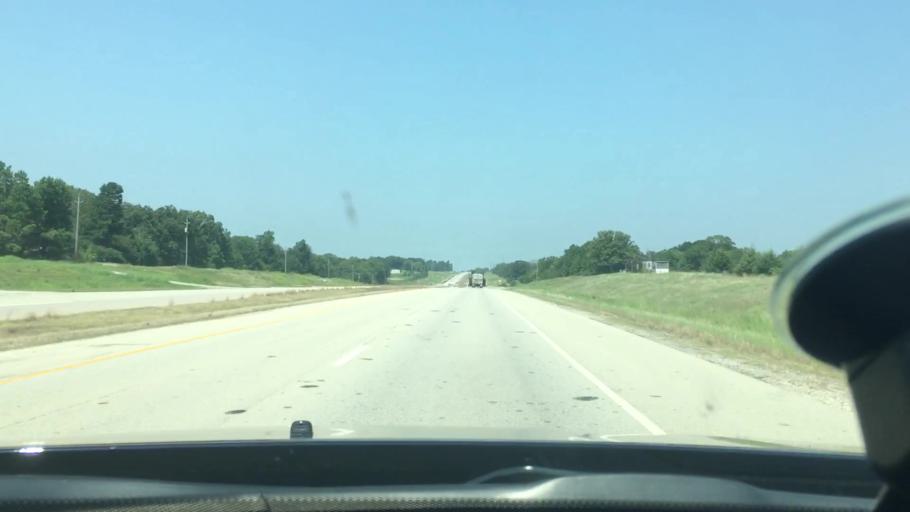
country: US
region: Oklahoma
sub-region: Atoka County
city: Atoka
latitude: 34.3203
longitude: -96.0362
